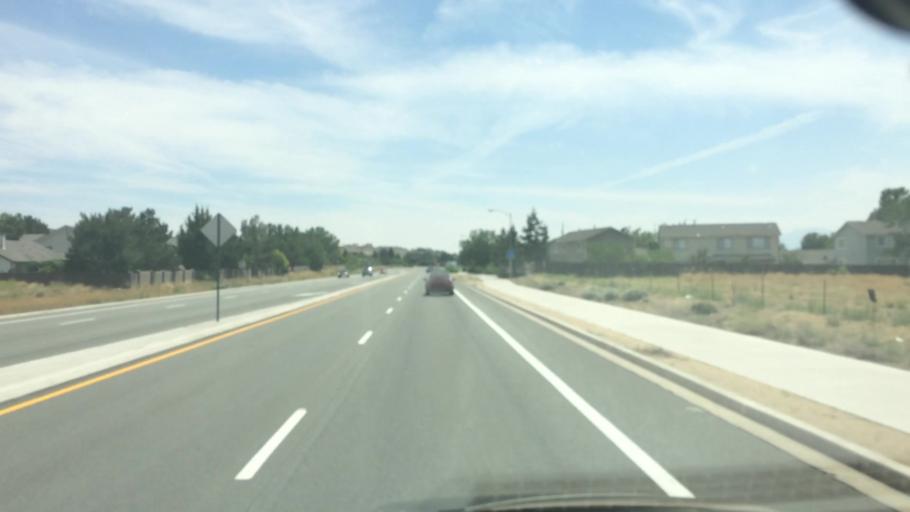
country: US
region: Nevada
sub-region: Washoe County
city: Spanish Springs
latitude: 39.5902
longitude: -119.7148
